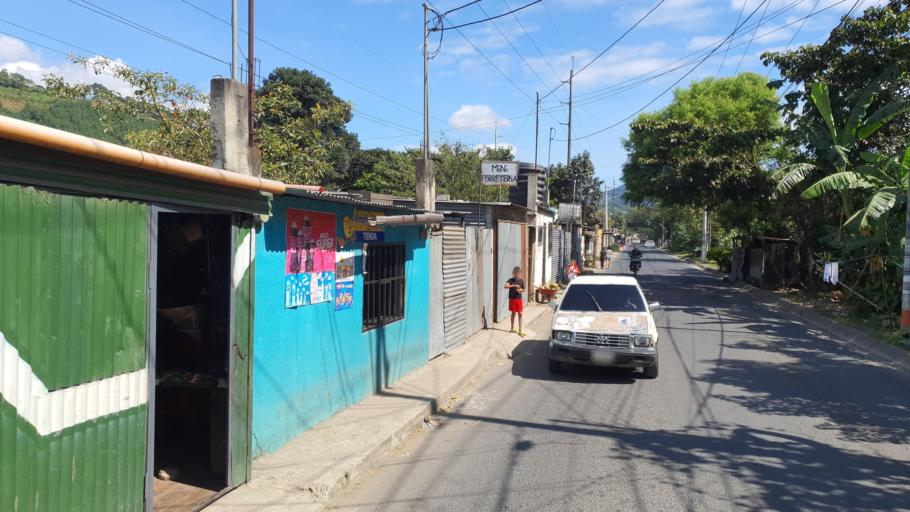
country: GT
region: Guatemala
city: Villa Canales
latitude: 14.4720
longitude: -90.5416
